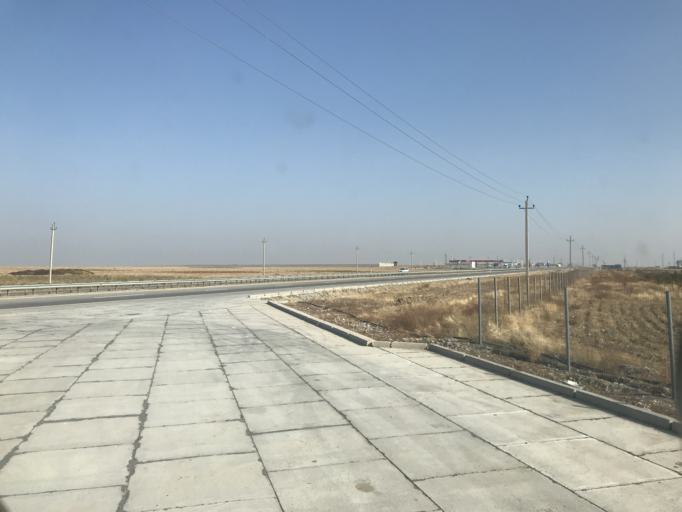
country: KZ
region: Ongtustik Qazaqstan
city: Shymkent
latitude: 42.4553
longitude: 69.6092
